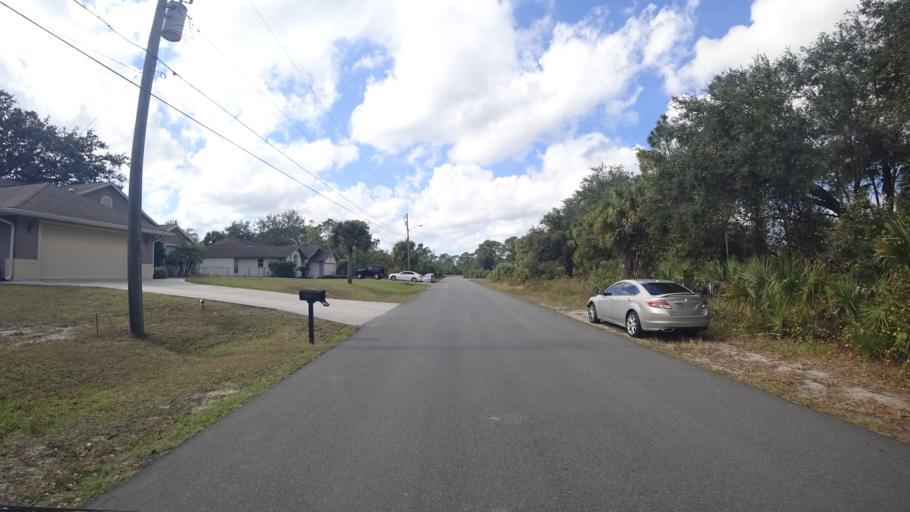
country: US
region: Florida
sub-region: Charlotte County
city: Port Charlotte
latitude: 27.0339
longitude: -82.1366
